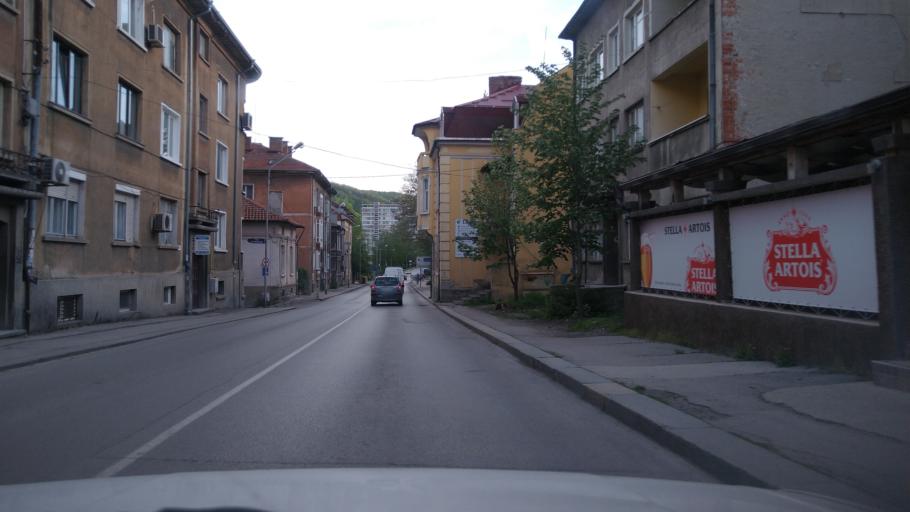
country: BG
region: Gabrovo
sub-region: Obshtina Gabrovo
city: Gabrovo
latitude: 42.8745
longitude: 25.3166
